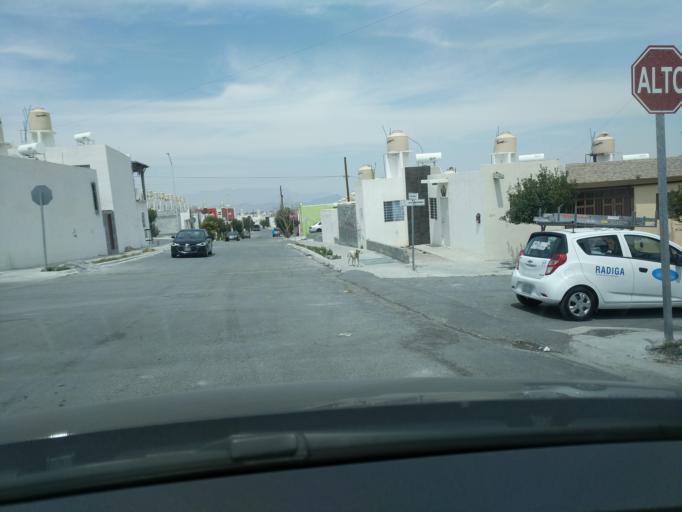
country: MX
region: Coahuila
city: Saltillo
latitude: 25.3459
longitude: -101.0062
